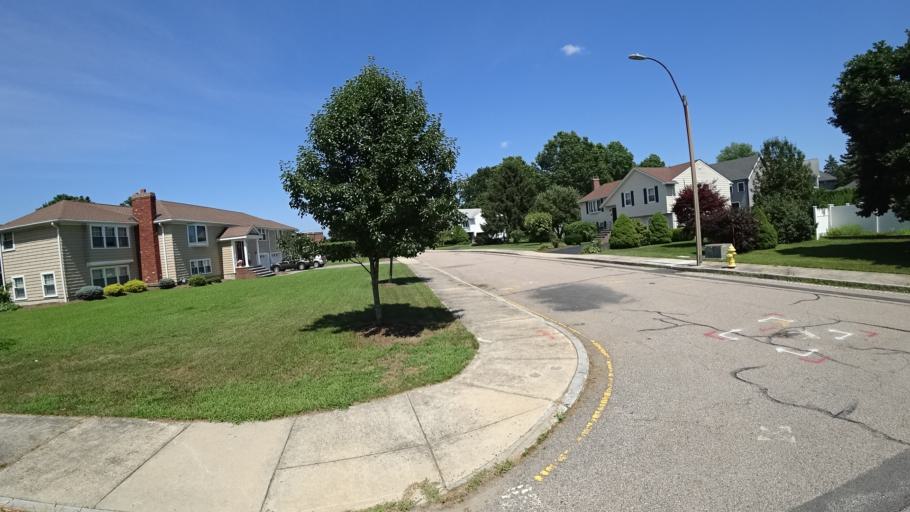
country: US
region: Massachusetts
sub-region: Norfolk County
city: Dedham
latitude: 42.2684
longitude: -71.1815
